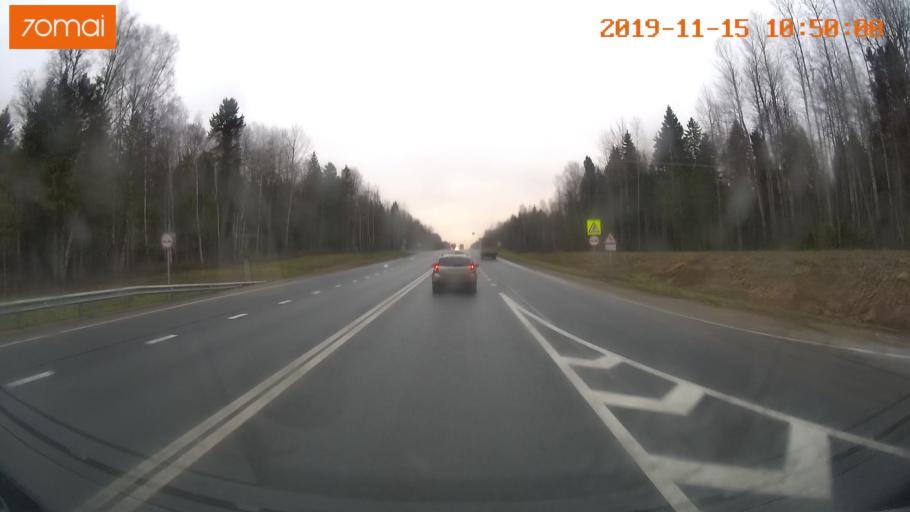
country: RU
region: Vologda
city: Sheksna
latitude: 59.1874
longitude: 38.6718
